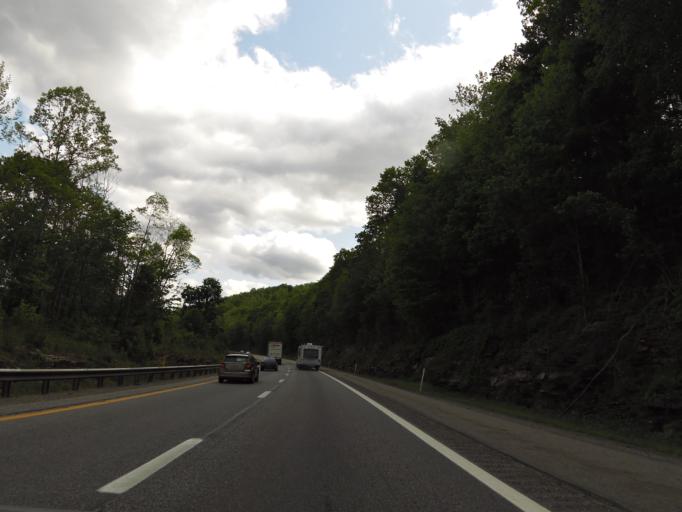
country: US
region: West Virginia
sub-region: Raleigh County
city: Prosperity
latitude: 37.8647
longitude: -81.2610
